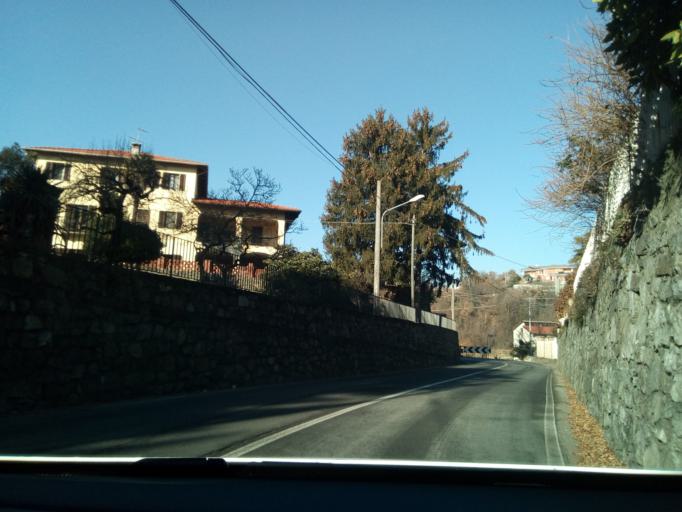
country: IT
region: Piedmont
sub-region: Provincia di Torino
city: Cascinette d'Ivrea
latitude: 45.4823
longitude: 7.8902
